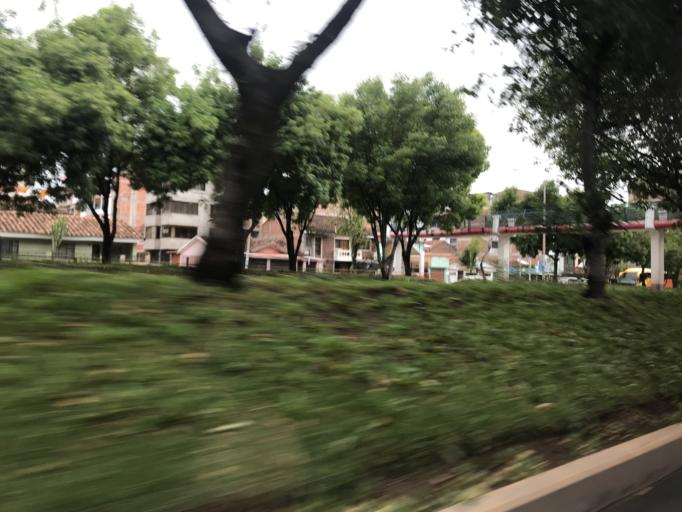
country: PE
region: Cusco
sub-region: Provincia de Cusco
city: Cusco
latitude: -13.5324
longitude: -71.9626
